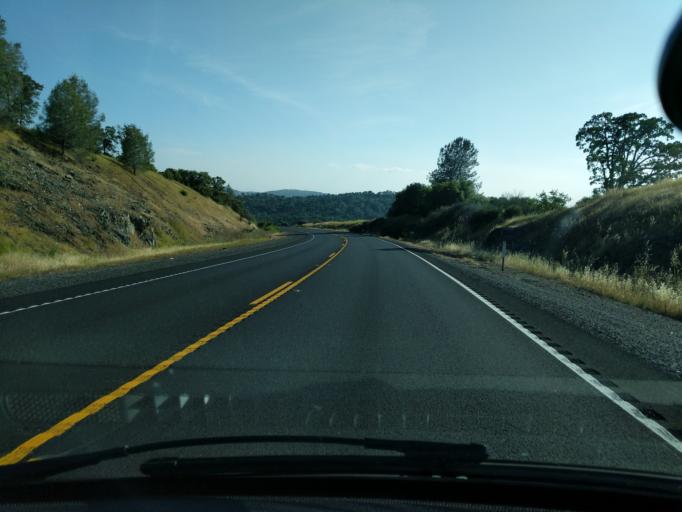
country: US
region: California
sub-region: Calaveras County
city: Copperopolis
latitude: 38.0027
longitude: -120.6490
